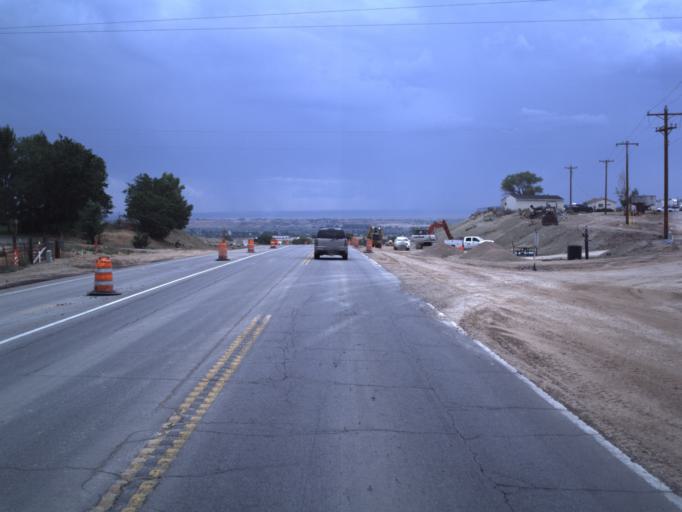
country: US
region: Utah
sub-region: Duchesne County
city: Roosevelt
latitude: 40.2344
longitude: -110.0675
